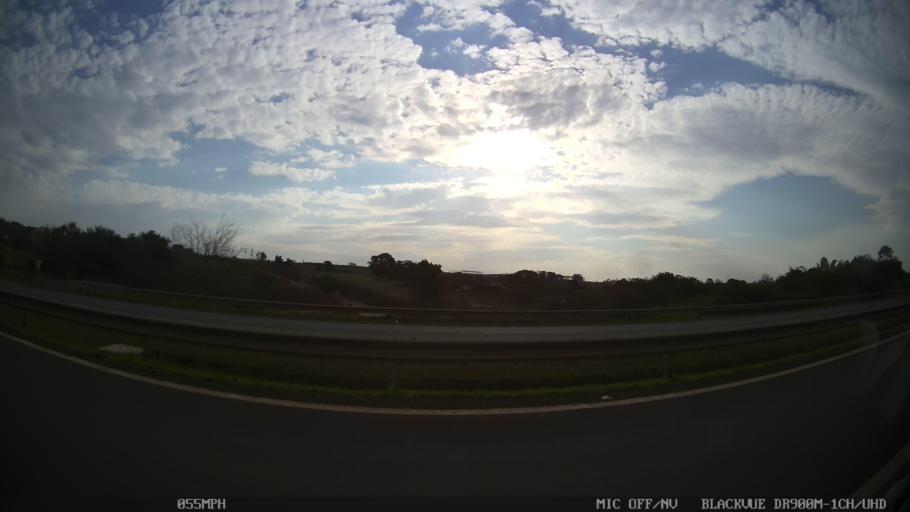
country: BR
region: Sao Paulo
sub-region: Cosmopolis
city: Cosmopolis
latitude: -22.6160
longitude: -47.1972
